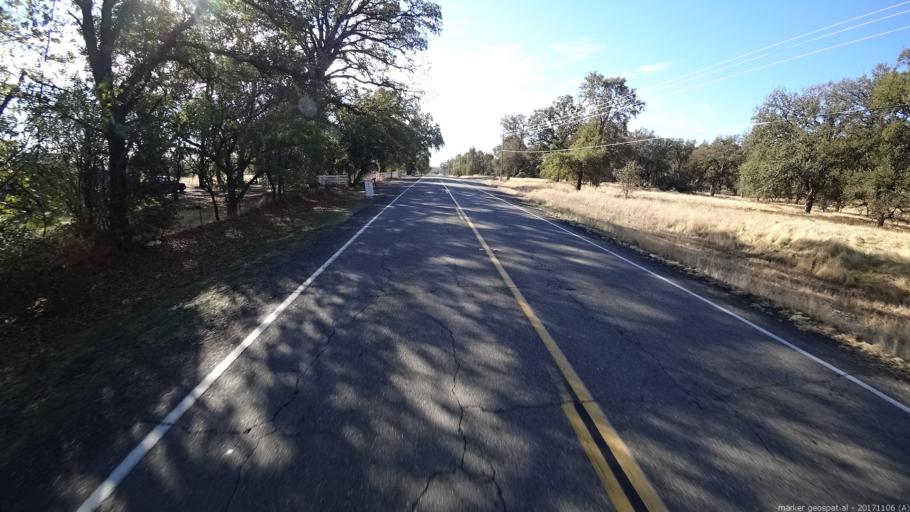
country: US
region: California
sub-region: Shasta County
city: Palo Cedro
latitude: 40.5154
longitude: -122.2385
